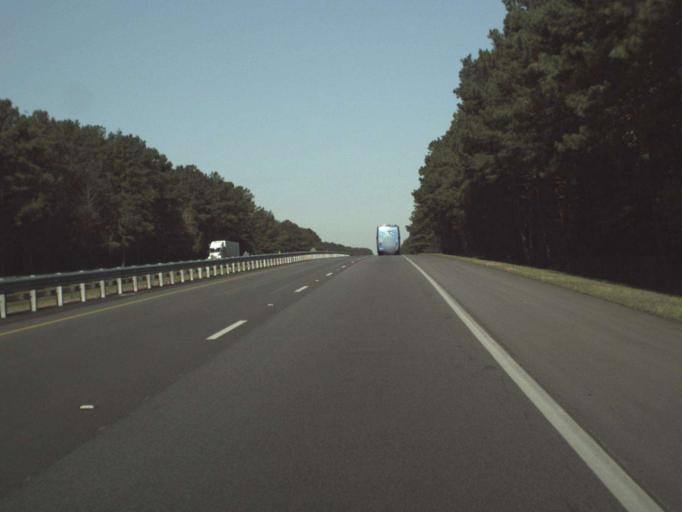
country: US
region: Florida
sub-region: Walton County
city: DeFuniak Springs
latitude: 30.6974
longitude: -86.1509
